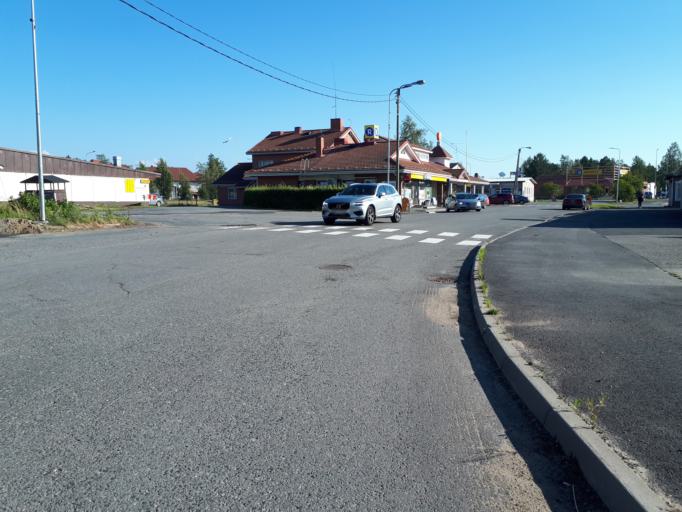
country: FI
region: Northern Ostrobothnia
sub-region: Oulunkaari
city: Ii
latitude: 65.3238
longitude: 25.3778
